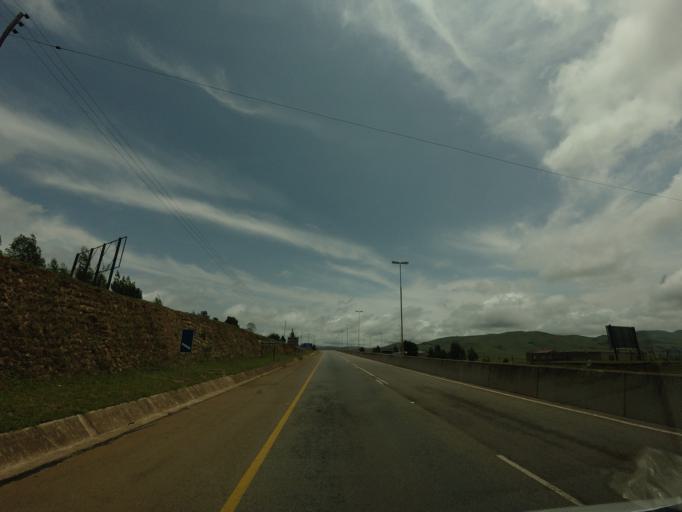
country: SZ
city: Darkton
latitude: -26.2458
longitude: 31.0590
